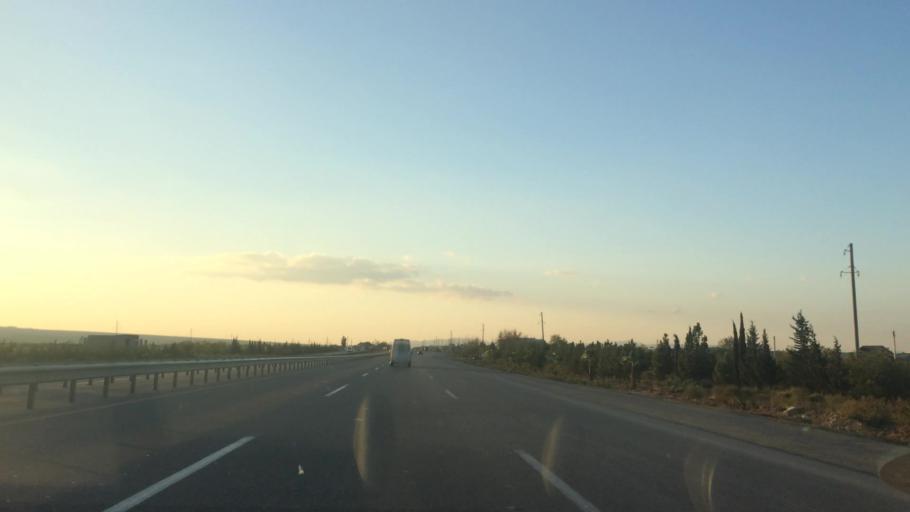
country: AZ
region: Haciqabul
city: Haciqabul
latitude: 40.0048
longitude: 49.1641
